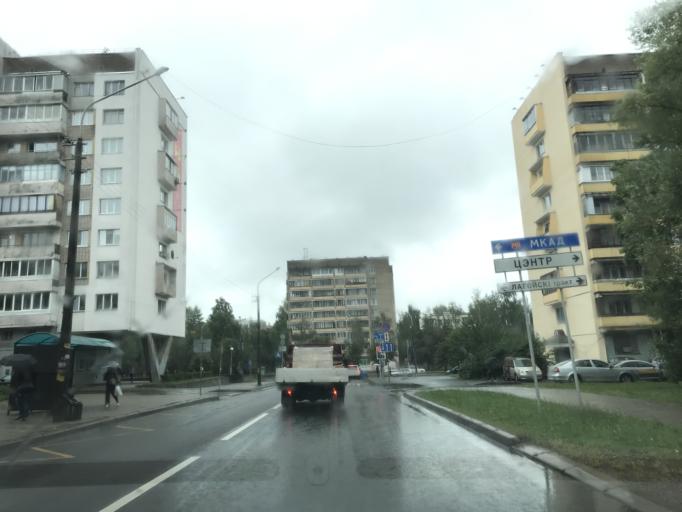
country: BY
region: Minsk
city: Bal'shavik
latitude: 53.9522
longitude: 27.6167
